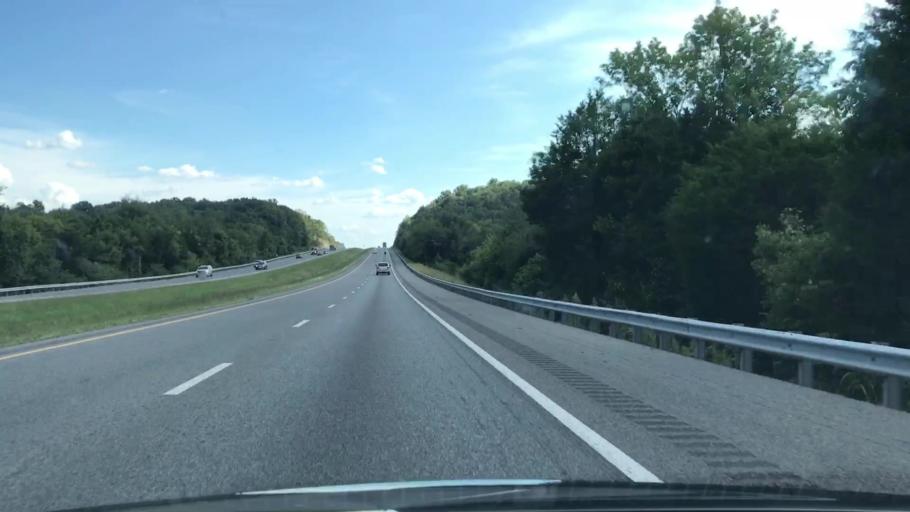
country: US
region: Alabama
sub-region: Limestone County
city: Ardmore
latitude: 35.0965
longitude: -86.8852
